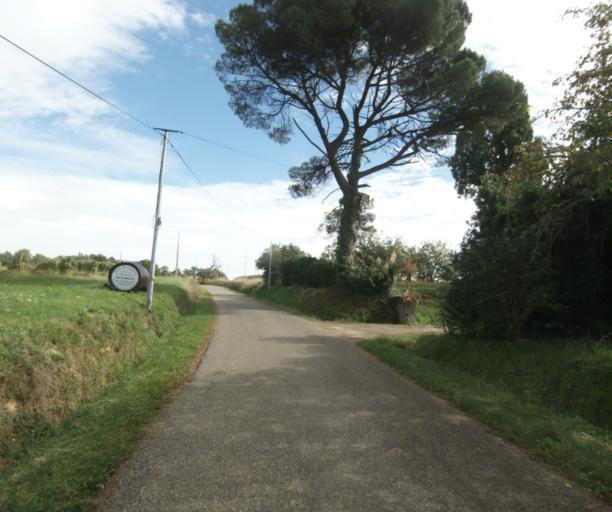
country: FR
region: Aquitaine
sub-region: Departement des Landes
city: Villeneuve-de-Marsan
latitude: 43.9009
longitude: -0.2076
